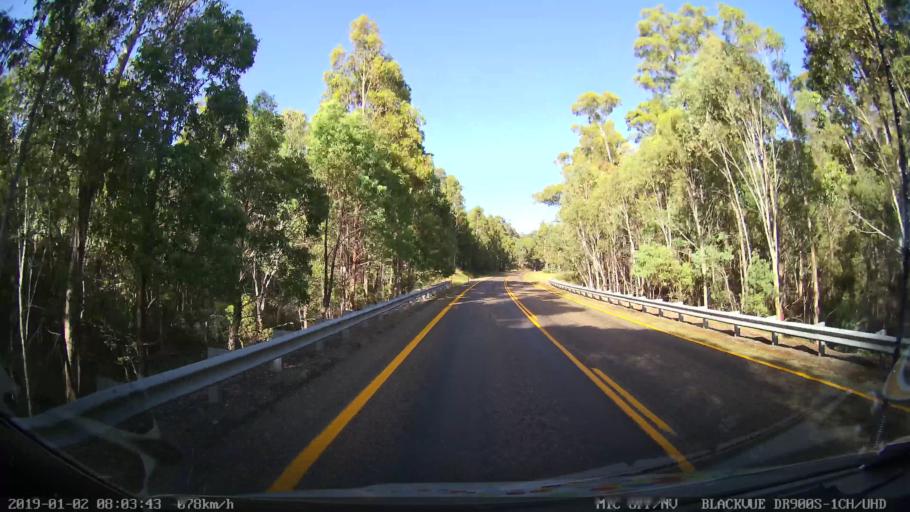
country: AU
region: New South Wales
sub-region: Tumut Shire
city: Tumut
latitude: -35.6636
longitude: 148.4045
